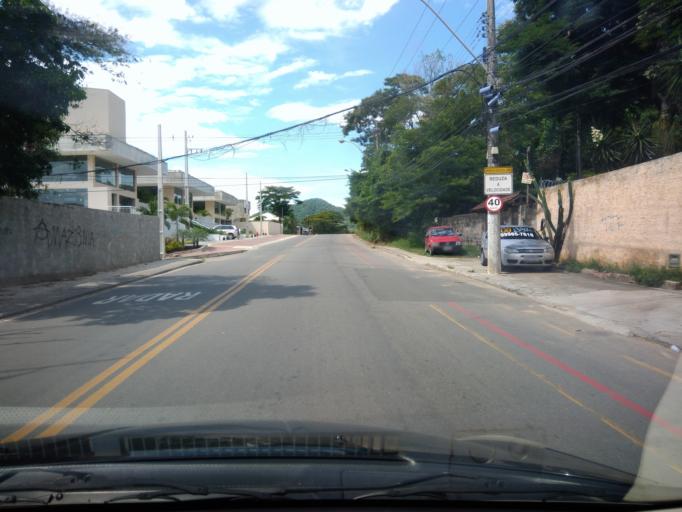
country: BR
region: Rio de Janeiro
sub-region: Niteroi
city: Niteroi
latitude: -22.9409
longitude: -43.0171
